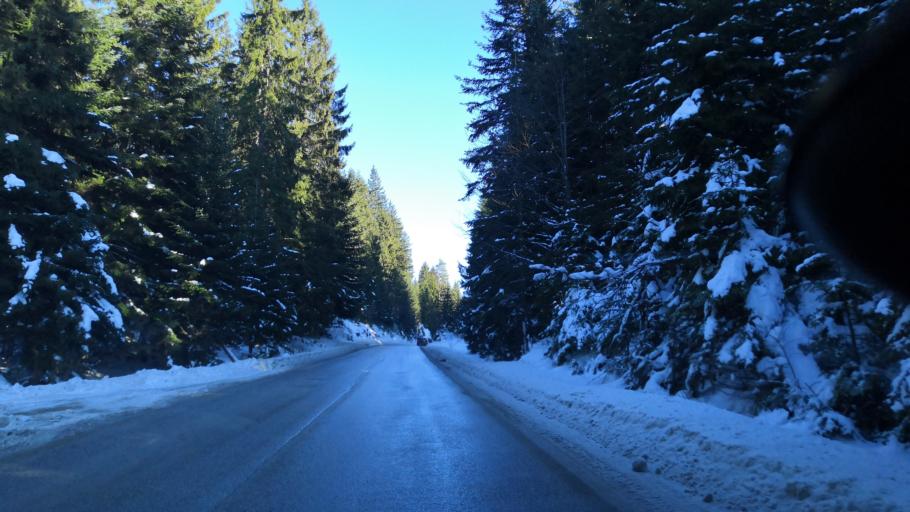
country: BA
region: Republika Srpska
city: Sokolac
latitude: 43.9260
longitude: 18.6652
